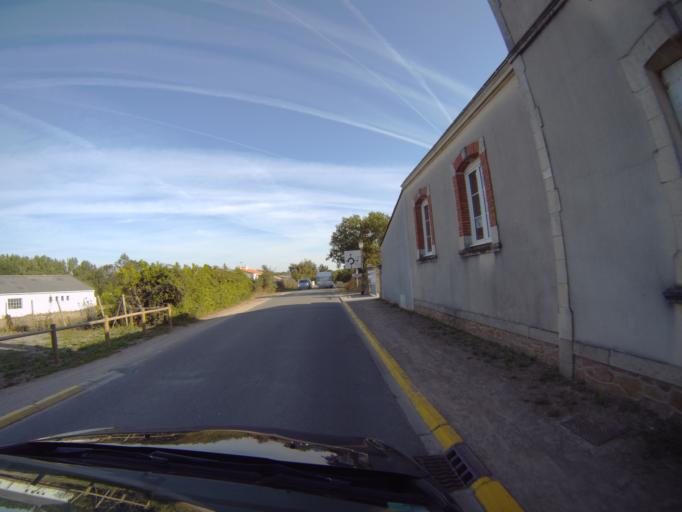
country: FR
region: Pays de la Loire
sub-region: Departement de la Vendee
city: Saint-Hilaire-de-Talmont
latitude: 46.4723
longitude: -1.6046
